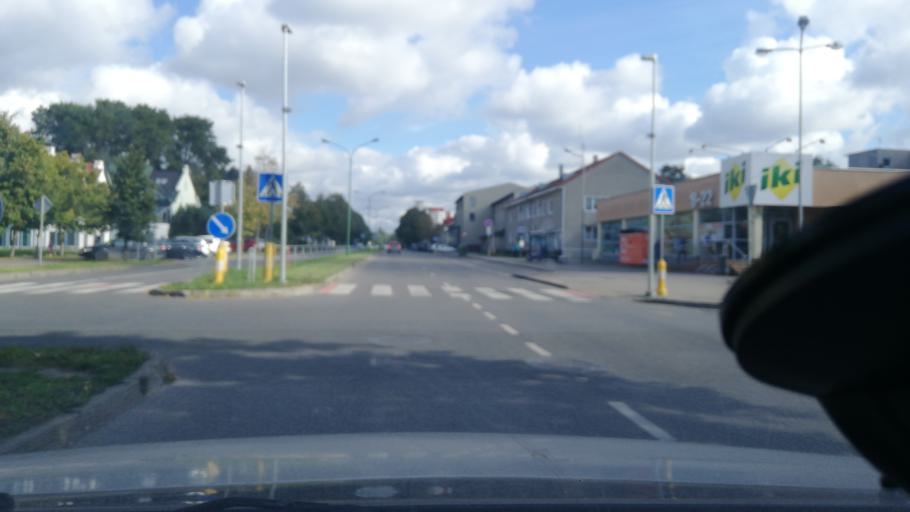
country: LT
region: Klaipedos apskritis
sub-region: Klaipeda
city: Klaipeda
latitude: 55.6787
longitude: 21.1557
